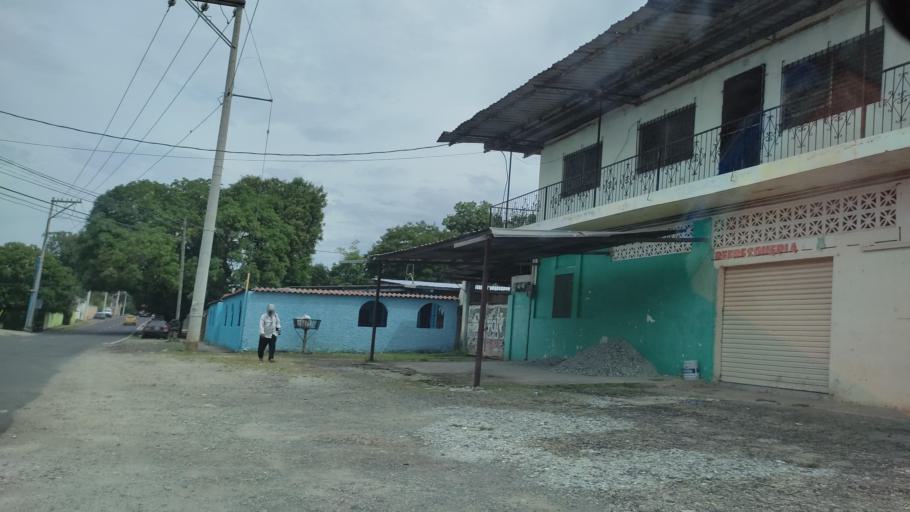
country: PA
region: Panama
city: San Miguelito
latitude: 9.0458
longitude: -79.4323
